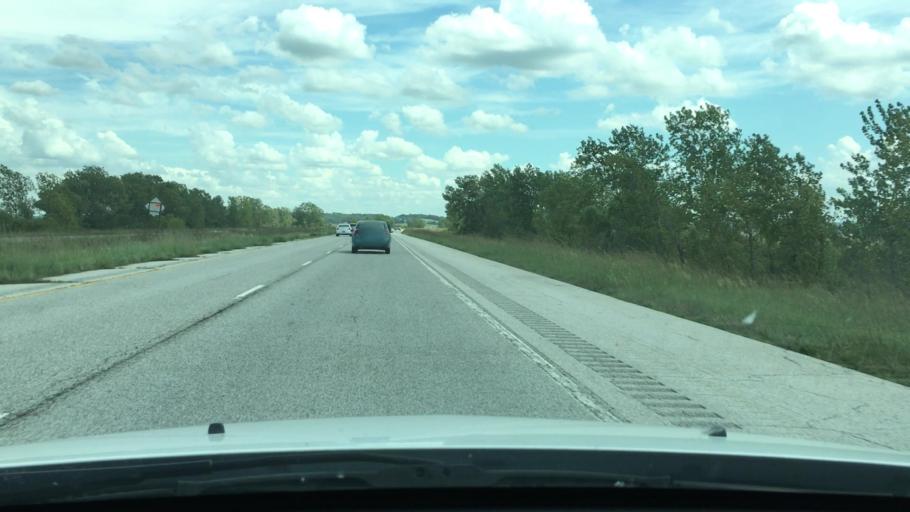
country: US
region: Illinois
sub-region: Pike County
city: Griggsville
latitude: 39.6917
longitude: -90.6153
